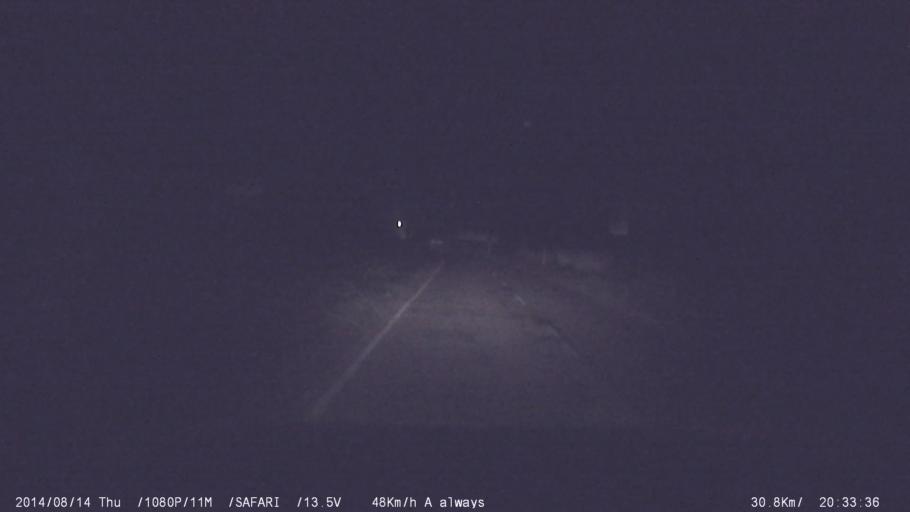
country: IN
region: Kerala
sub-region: Kottayam
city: Palackattumala
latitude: 9.7247
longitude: 76.5611
